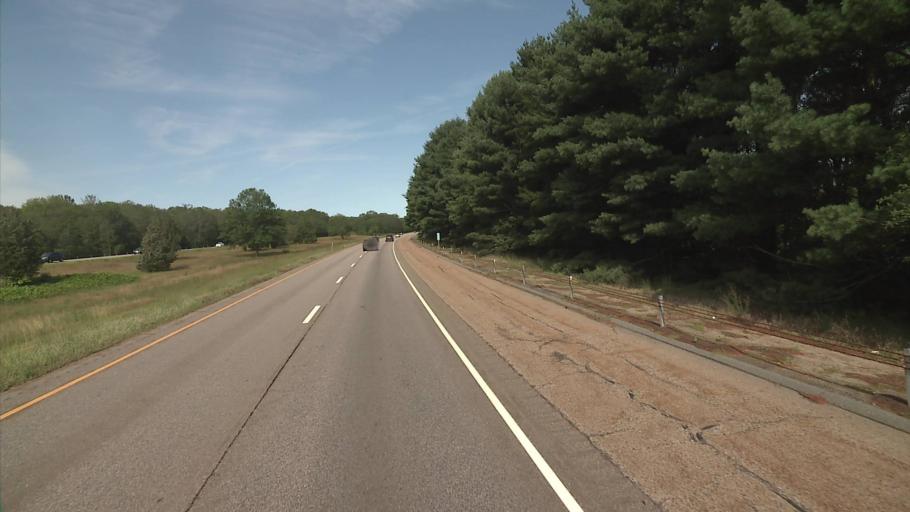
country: US
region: Connecticut
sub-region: New London County
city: Colchester
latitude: 41.5657
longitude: -72.2435
